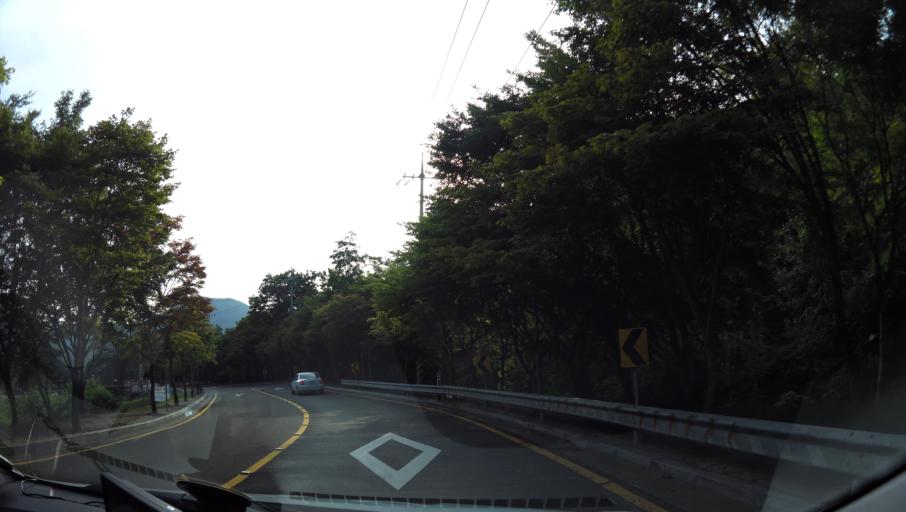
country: KR
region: Daegu
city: Daegu
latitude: 35.9864
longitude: 128.6540
